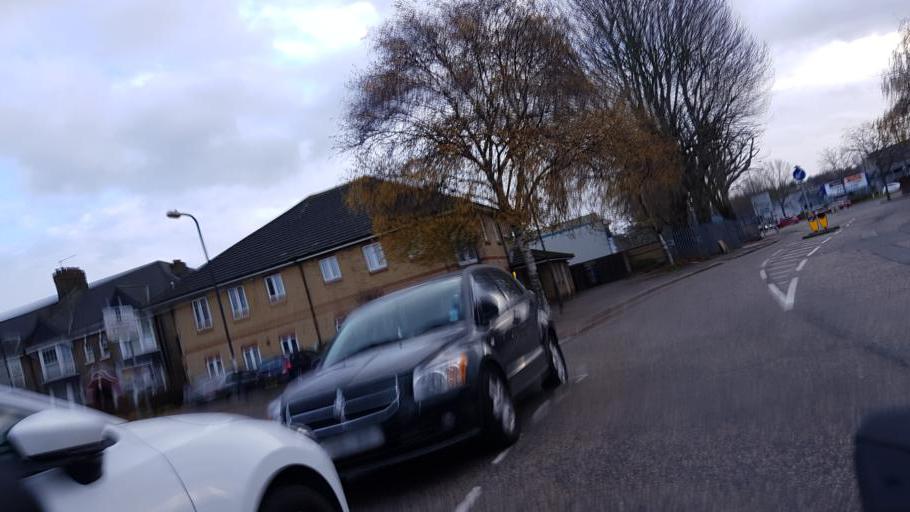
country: GB
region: England
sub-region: Greater London
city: Blackheath
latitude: 51.4914
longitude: 0.0300
